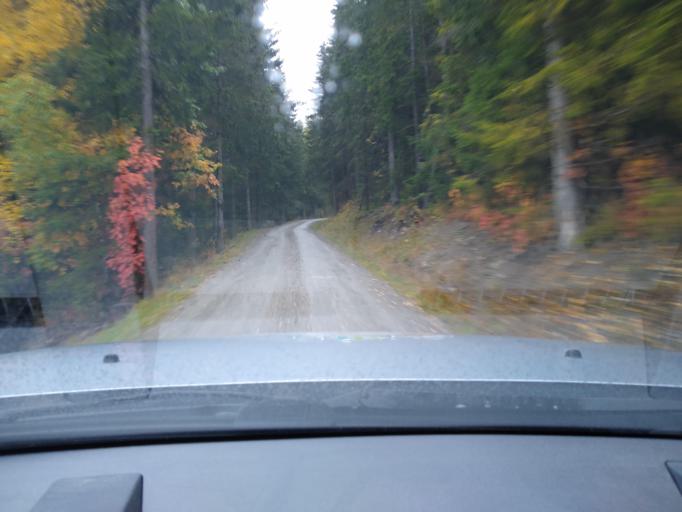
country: NO
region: Oppland
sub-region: Ringebu
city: Ringebu
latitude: 61.5506
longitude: 10.1493
